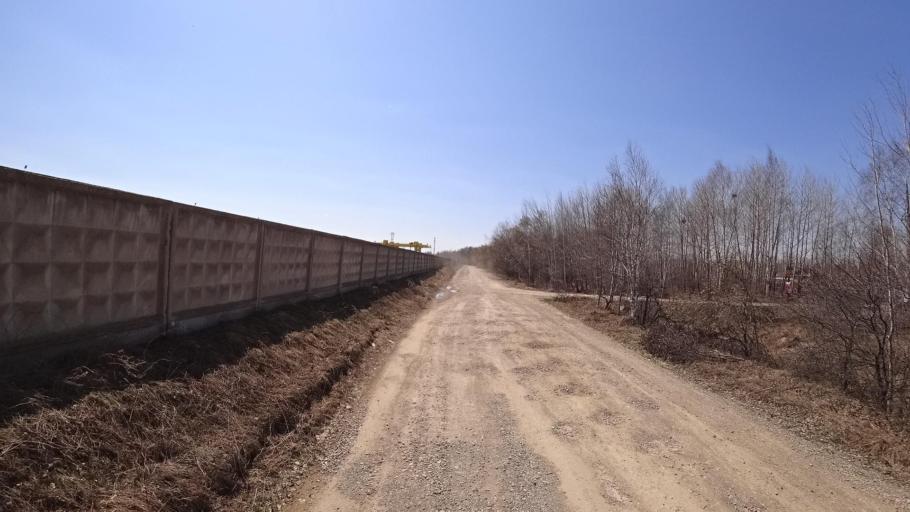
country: RU
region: Khabarovsk Krai
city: Khurba
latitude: 50.4167
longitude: 136.8853
